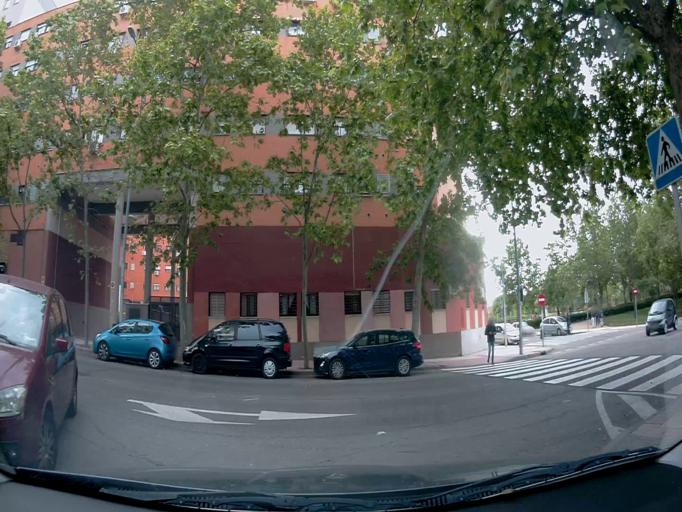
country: ES
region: Madrid
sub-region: Provincia de Madrid
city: Alcorcon
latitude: 40.3362
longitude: -3.8342
